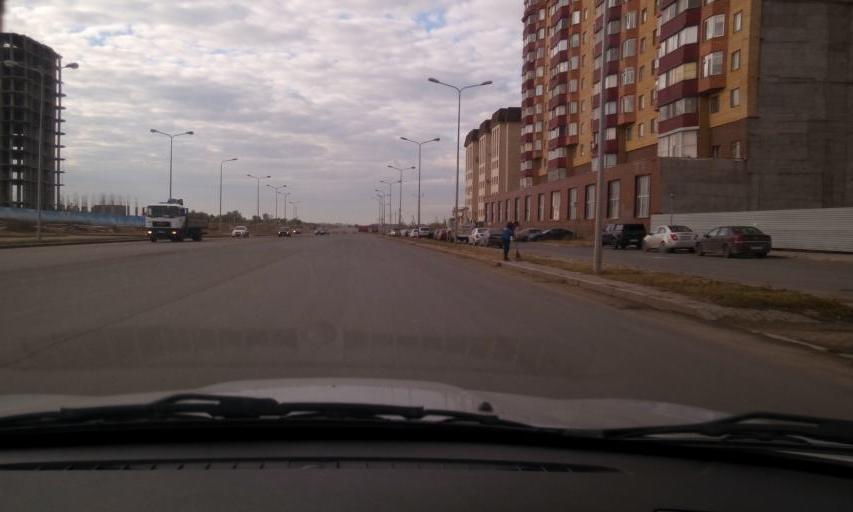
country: KZ
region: Astana Qalasy
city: Astana
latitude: 51.1241
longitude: 71.4868
